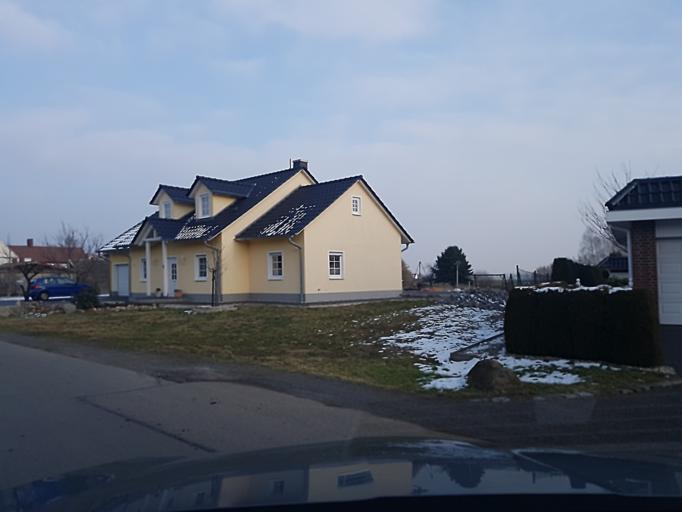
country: DE
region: Brandenburg
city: Schonborn
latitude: 51.5930
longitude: 13.4927
